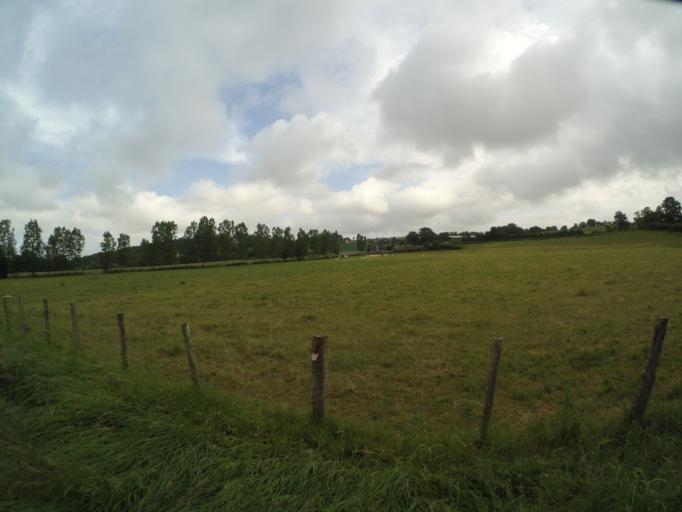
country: FR
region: Pays de la Loire
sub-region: Departement de la Vendee
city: Nesmy
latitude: 46.6155
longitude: -1.4021
